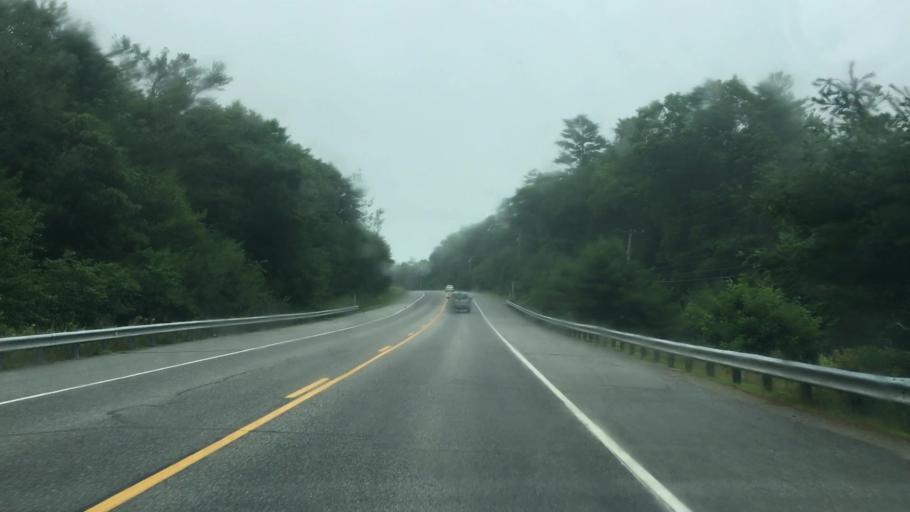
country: US
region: Maine
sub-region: Lincoln County
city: Edgecomb
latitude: 43.9404
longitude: -69.6259
